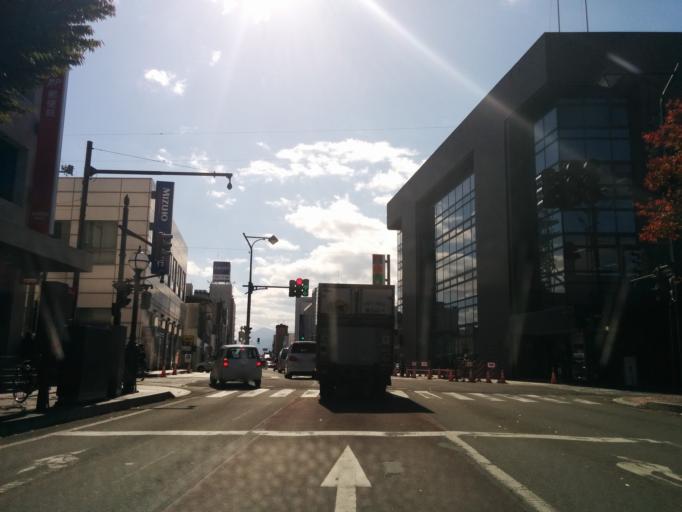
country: JP
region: Fukushima
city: Kitakata
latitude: 37.4987
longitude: 139.9288
